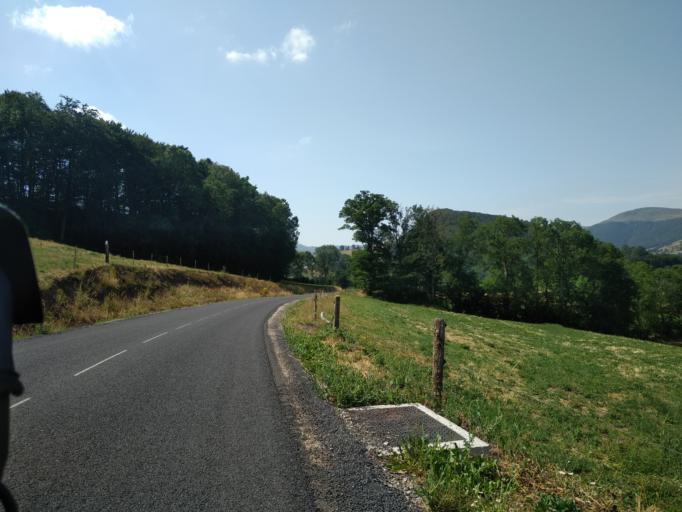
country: FR
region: Auvergne
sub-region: Departement du Cantal
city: Riom-es-Montagnes
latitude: 45.1921
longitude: 2.7159
